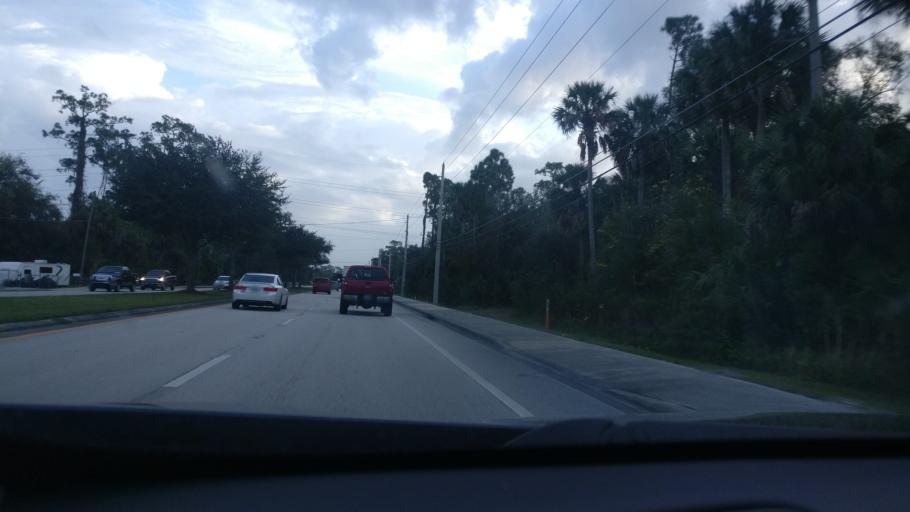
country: US
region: Florida
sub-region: Volusia County
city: DeBary
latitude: 28.8508
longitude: -81.3223
